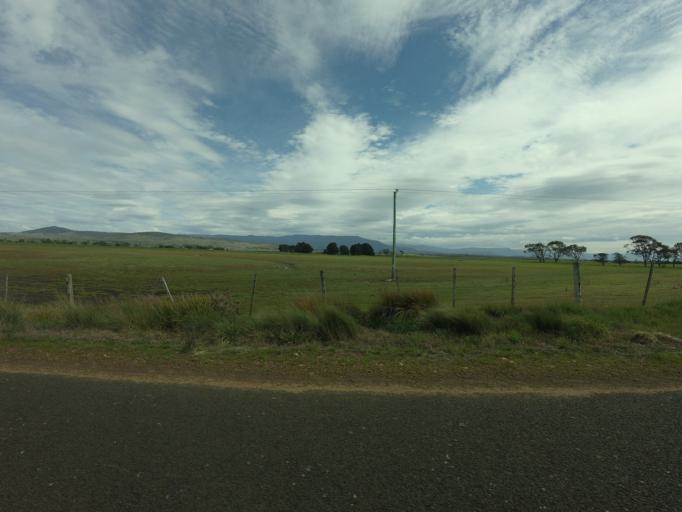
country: AU
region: Tasmania
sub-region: Northern Midlands
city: Evandale
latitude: -41.8537
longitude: 147.3416
